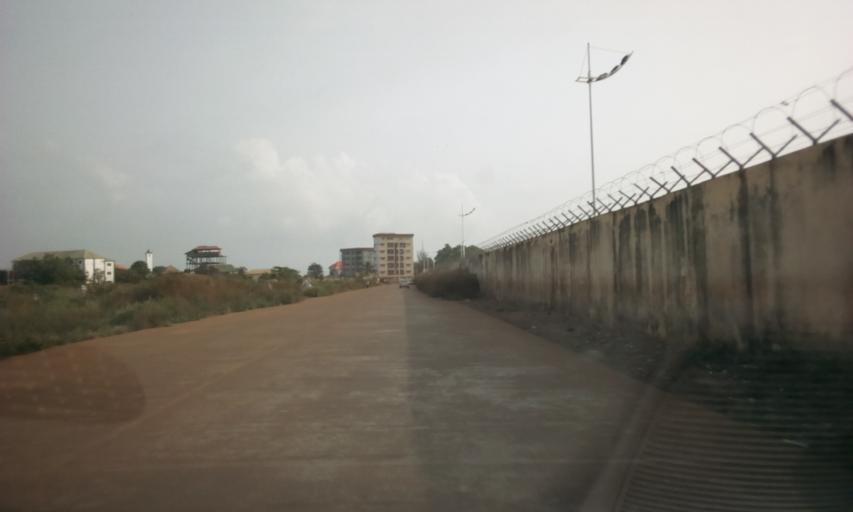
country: GN
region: Conakry
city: Conakry
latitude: 9.6252
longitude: -13.6285
